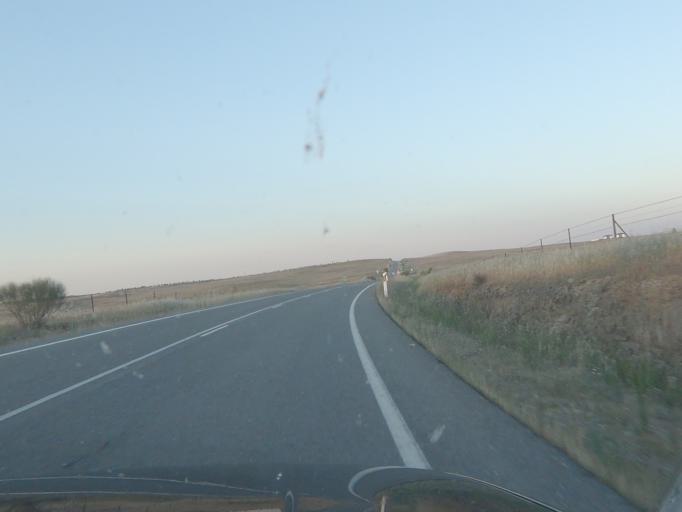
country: ES
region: Extremadura
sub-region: Provincia de Caceres
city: Salorino
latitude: 39.6072
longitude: -6.9707
